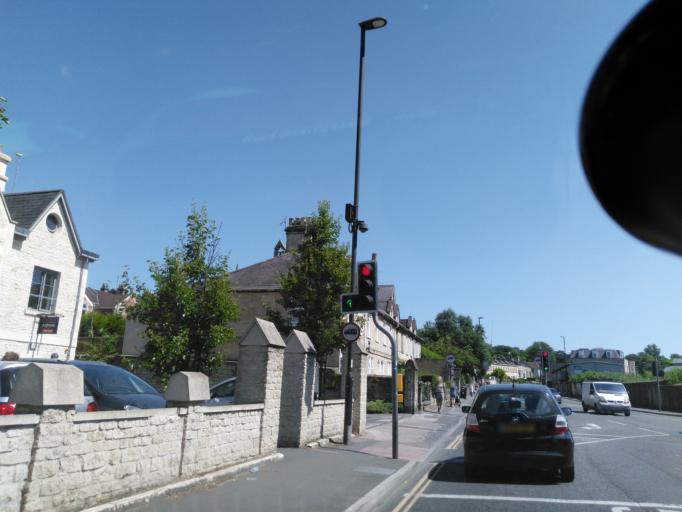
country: GB
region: England
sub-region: Bath and North East Somerset
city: Bath
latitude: 51.3847
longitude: -2.3820
